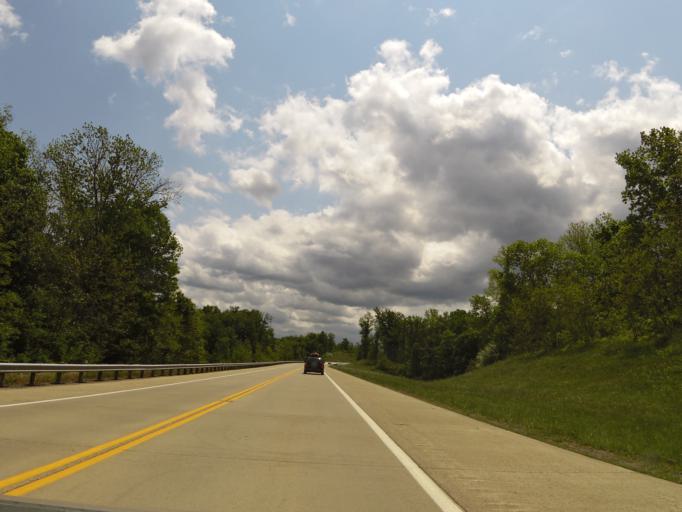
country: US
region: Ohio
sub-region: Athens County
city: Athens
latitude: 39.2101
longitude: -82.0591
